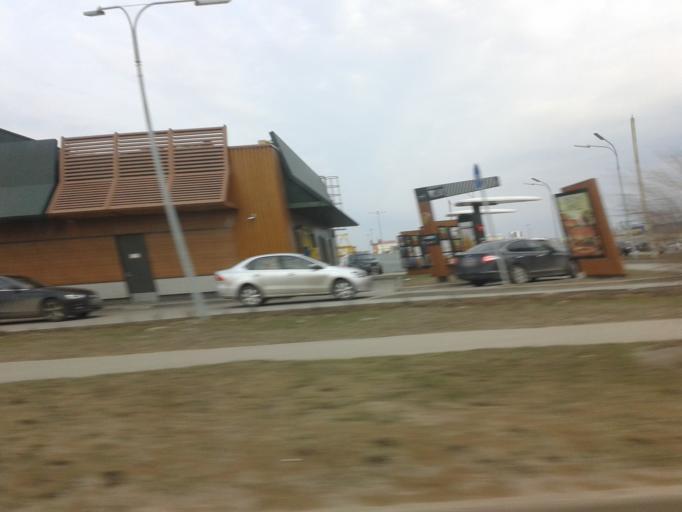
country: RU
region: Rjazan
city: Ryazan'
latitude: 54.6380
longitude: 39.6781
